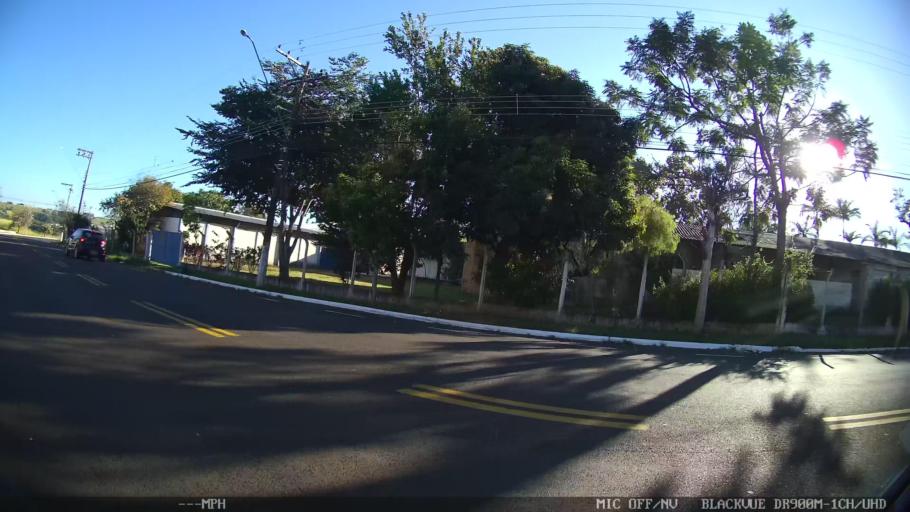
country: BR
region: Sao Paulo
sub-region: Franca
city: Franca
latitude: -20.5623
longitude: -47.4094
